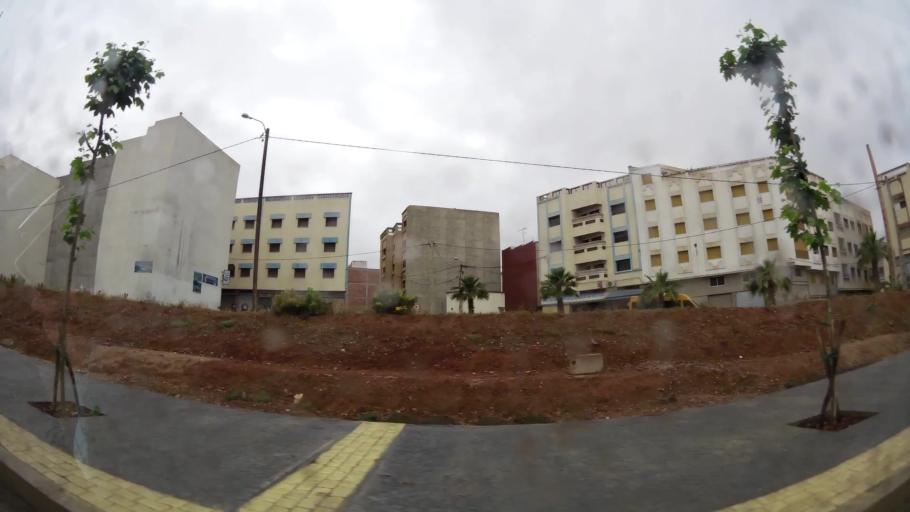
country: MA
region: Taza-Al Hoceima-Taounate
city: Imzourene
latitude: 35.1415
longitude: -3.8482
